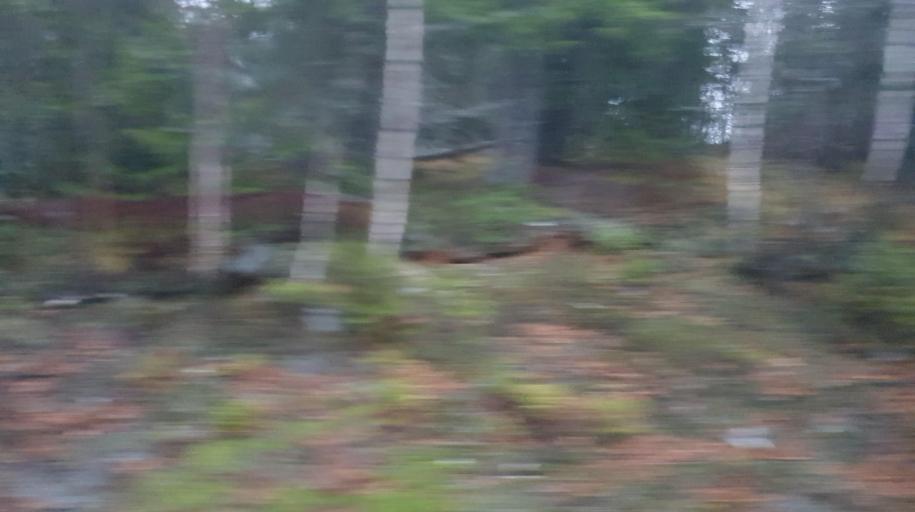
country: NO
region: Buskerud
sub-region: Krodsherad
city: Noresund
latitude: 60.2157
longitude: 9.5458
